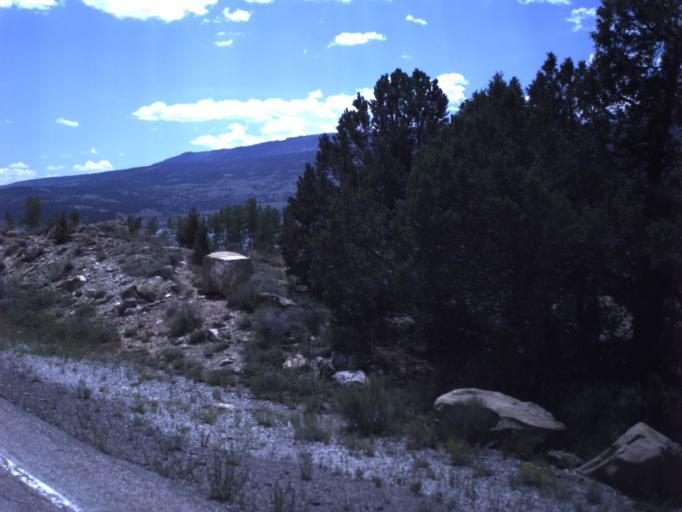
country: US
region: Utah
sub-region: Emery County
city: Orangeville
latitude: 39.3045
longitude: -111.2727
